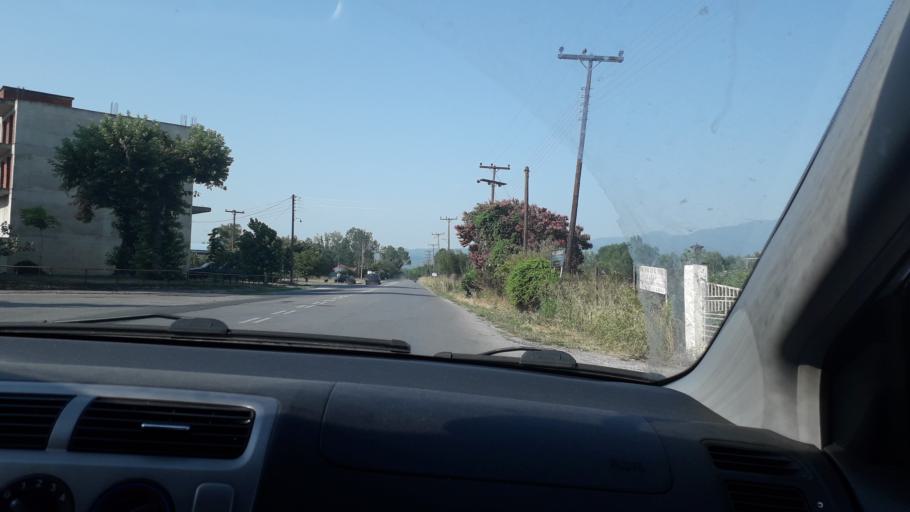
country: GR
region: Central Macedonia
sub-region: Nomos Pellis
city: Aridaia
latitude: 40.9672
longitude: 22.0542
